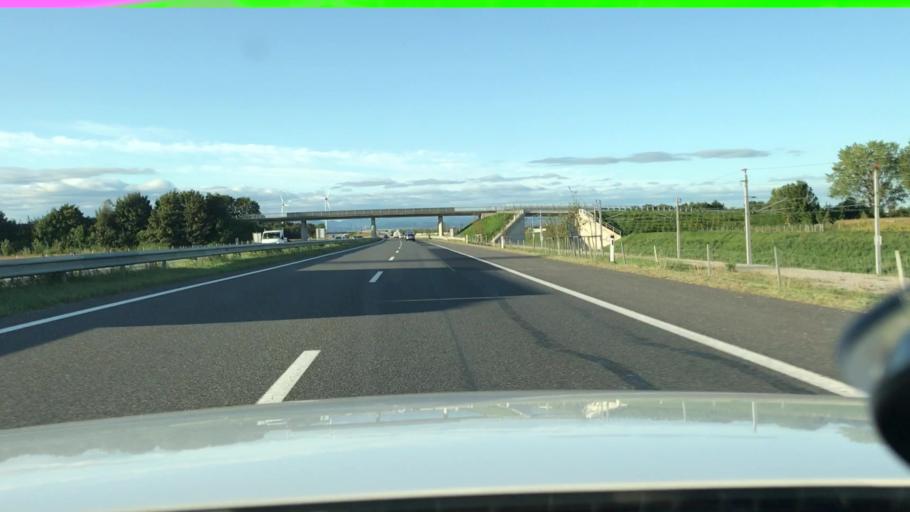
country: AT
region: Lower Austria
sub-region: Sankt Polten Stadt
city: Sankt Poelten
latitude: 48.2070
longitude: 15.6663
